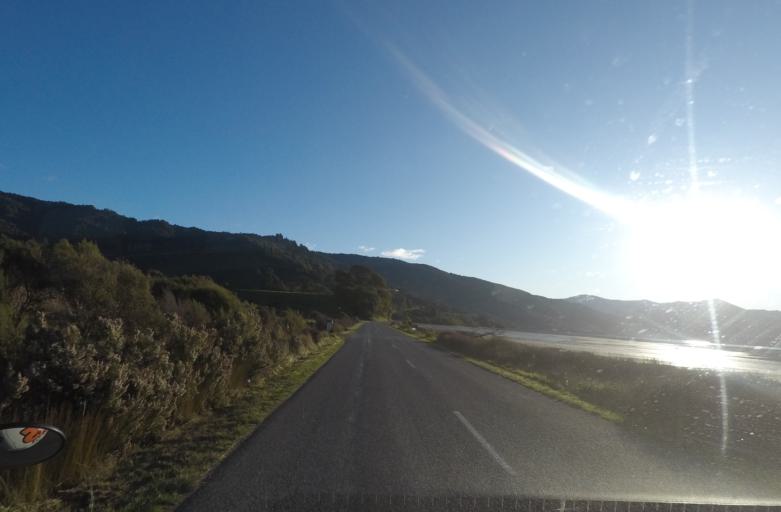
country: NZ
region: Marlborough
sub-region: Marlborough District
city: Picton
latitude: -41.2925
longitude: 173.8279
